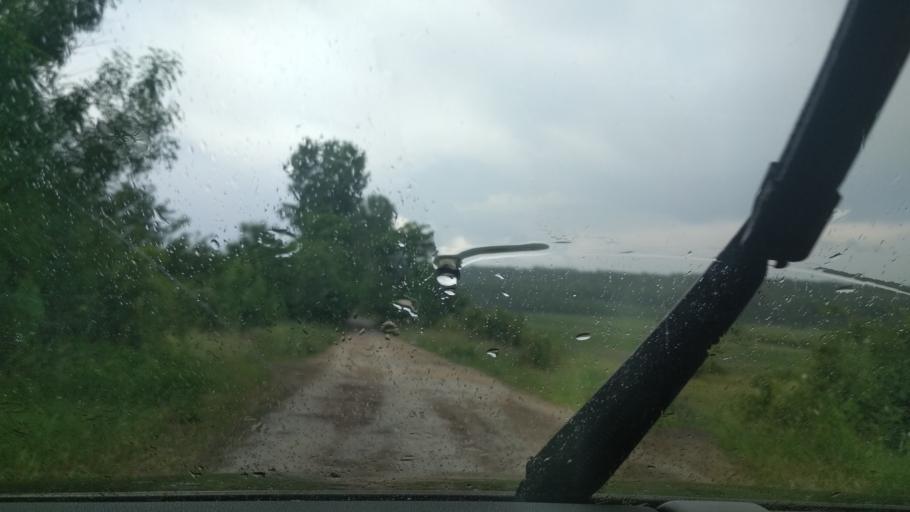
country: MD
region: Singerei
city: Biruinta
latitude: 47.7437
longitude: 28.1376
